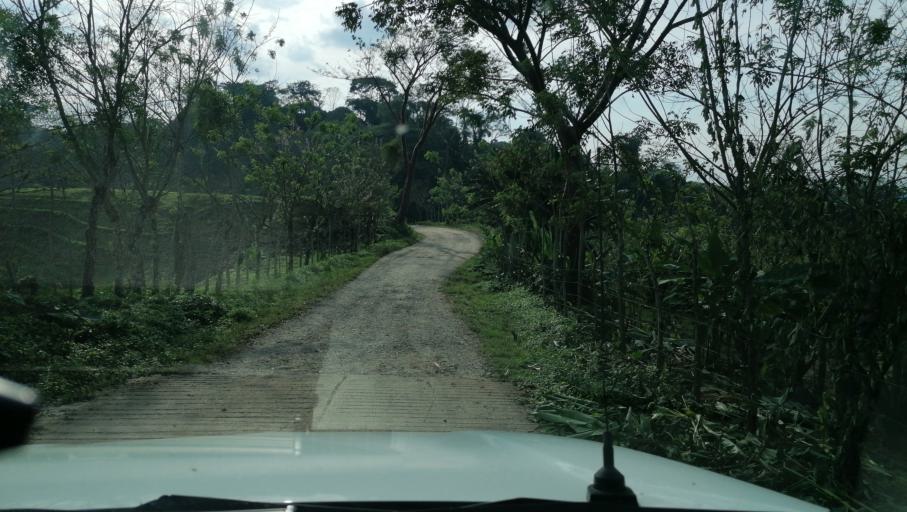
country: MX
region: Chiapas
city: Pichucalco
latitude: 17.4841
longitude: -93.2307
